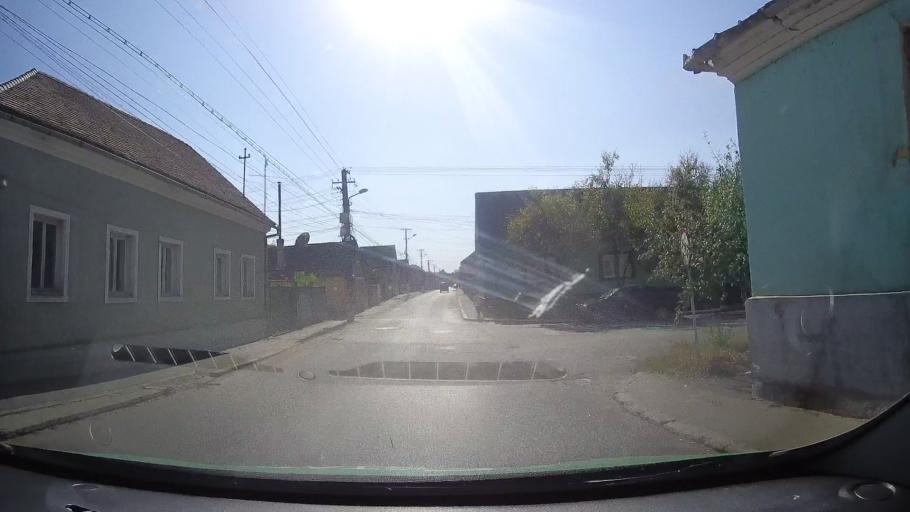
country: RO
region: Arad
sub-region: Oras Lipova
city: Lipova
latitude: 46.0872
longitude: 21.6908
